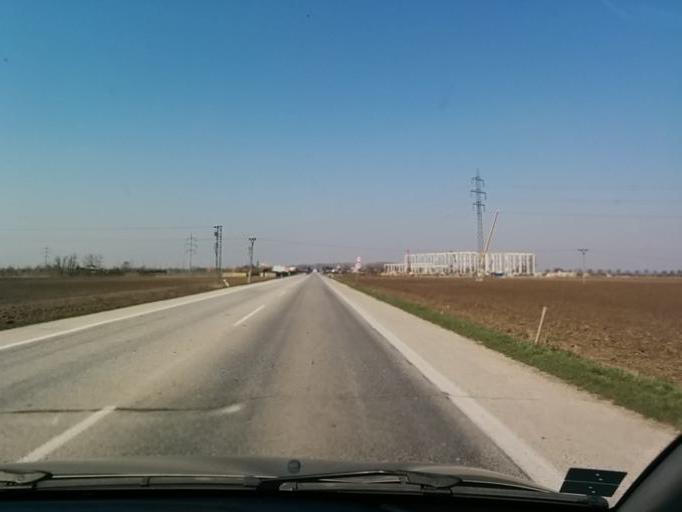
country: SK
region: Trnavsky
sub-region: Okres Galanta
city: Galanta
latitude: 48.2059
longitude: 17.7306
